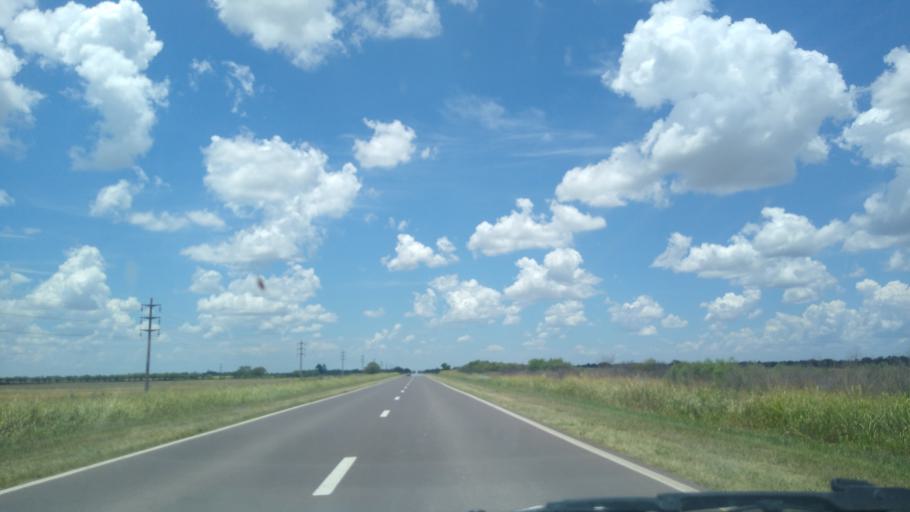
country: AR
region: Chaco
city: Presidencia Roque Saenz Pena
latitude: -26.7327
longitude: -60.3834
